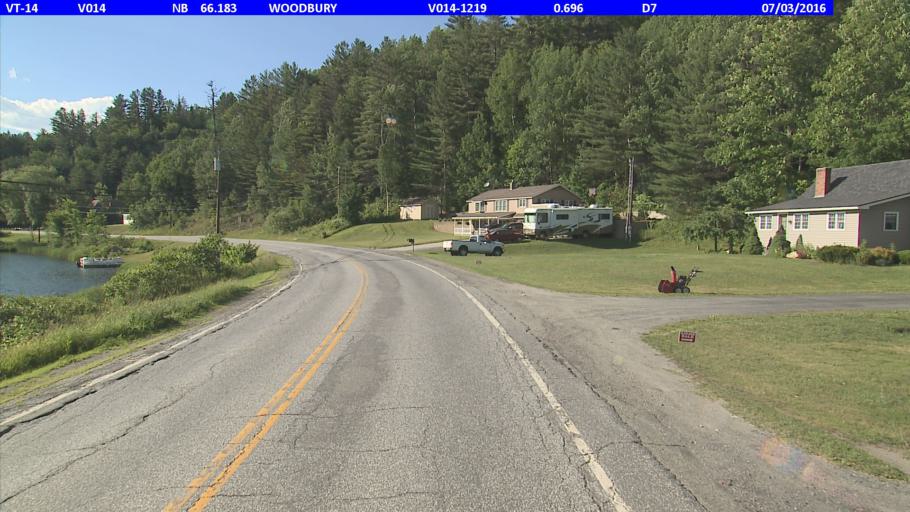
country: US
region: Vermont
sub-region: Caledonia County
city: Hardwick
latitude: 44.4054
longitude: -72.4101
